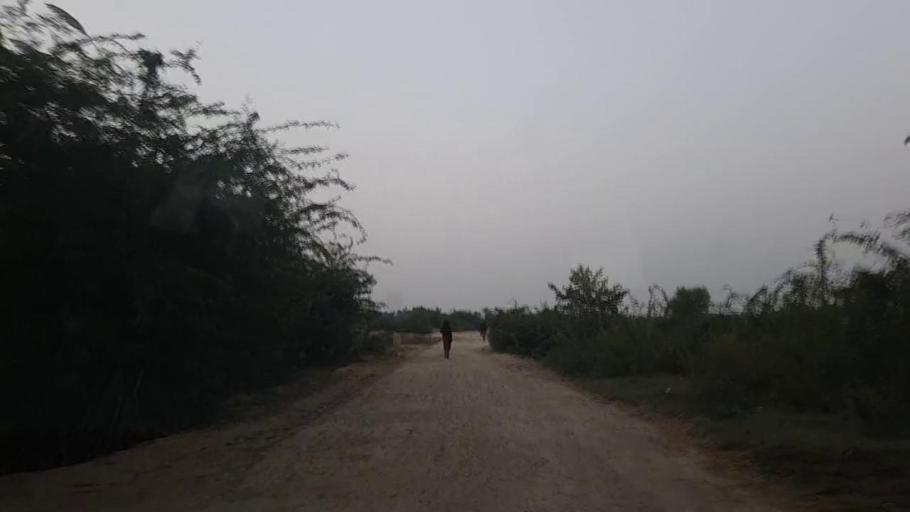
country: PK
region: Sindh
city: Mirpur Sakro
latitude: 24.5854
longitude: 67.7841
